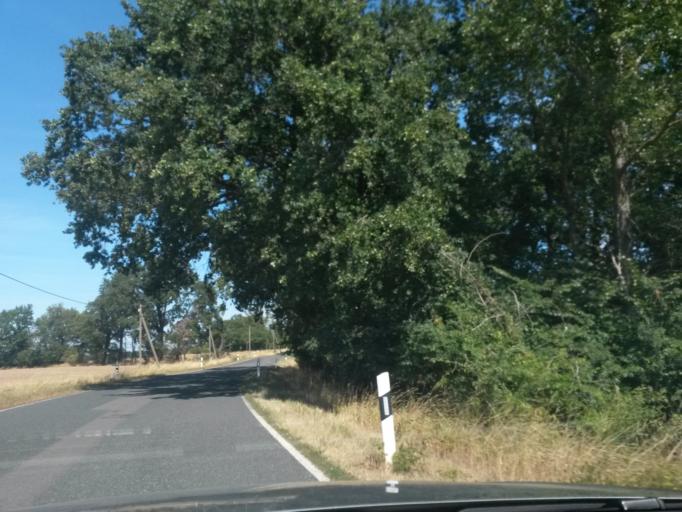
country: DE
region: Saxony-Anhalt
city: Pretzsch
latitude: 51.7353
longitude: 12.8288
